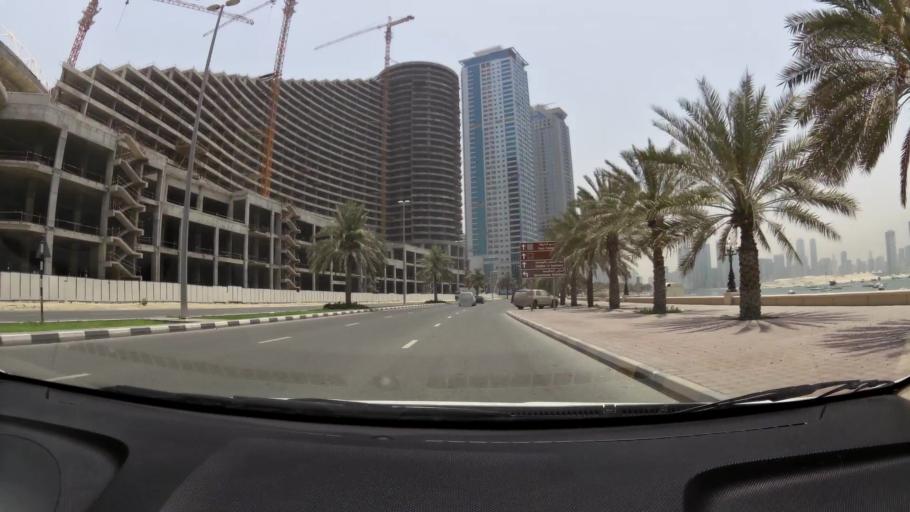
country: AE
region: Ash Shariqah
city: Sharjah
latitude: 25.3308
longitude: 55.3622
